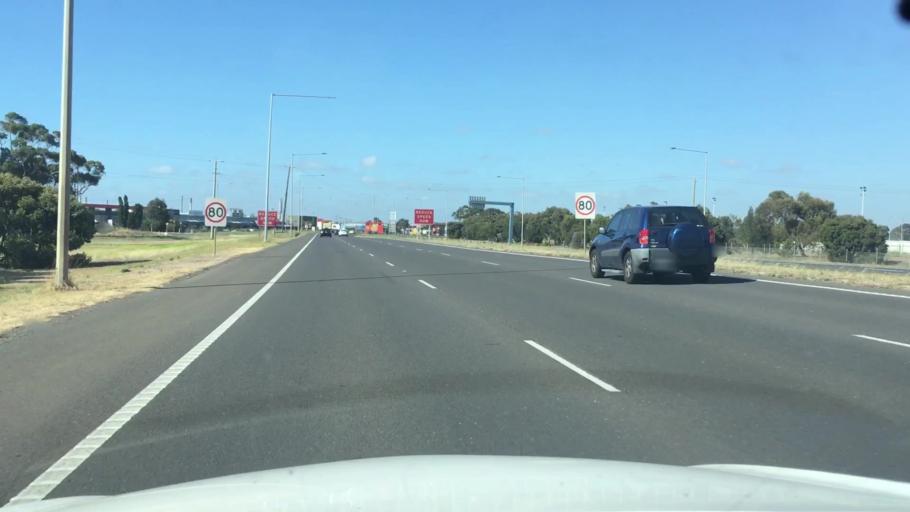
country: AU
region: Victoria
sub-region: Greater Geelong
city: Lara
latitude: -38.0602
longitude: 144.3854
